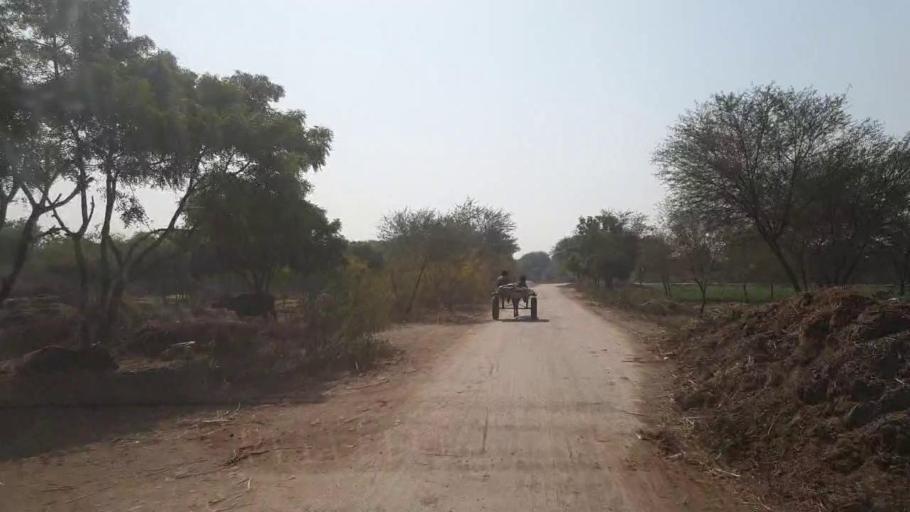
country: PK
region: Sindh
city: Tando Jam
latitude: 25.3316
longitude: 68.6249
